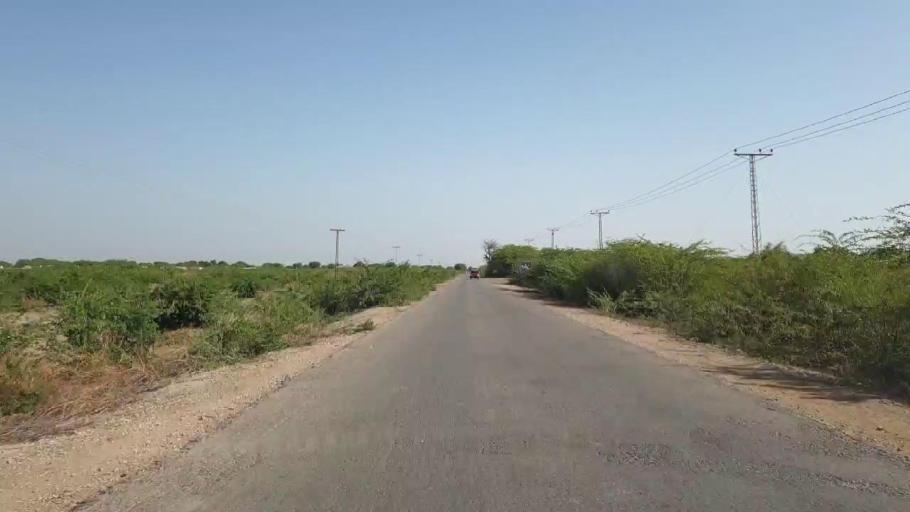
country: PK
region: Sindh
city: Umarkot
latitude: 25.4298
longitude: 69.7420
